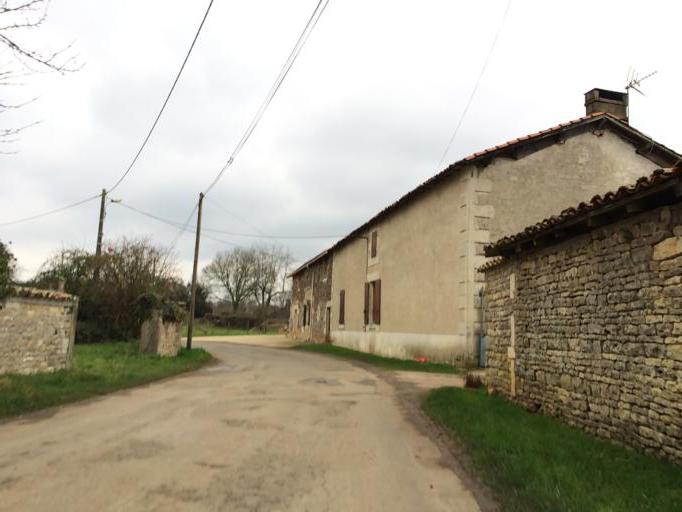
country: FR
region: Poitou-Charentes
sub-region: Departement des Deux-Sevres
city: Sauze-Vaussais
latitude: 46.1567
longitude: 0.1456
